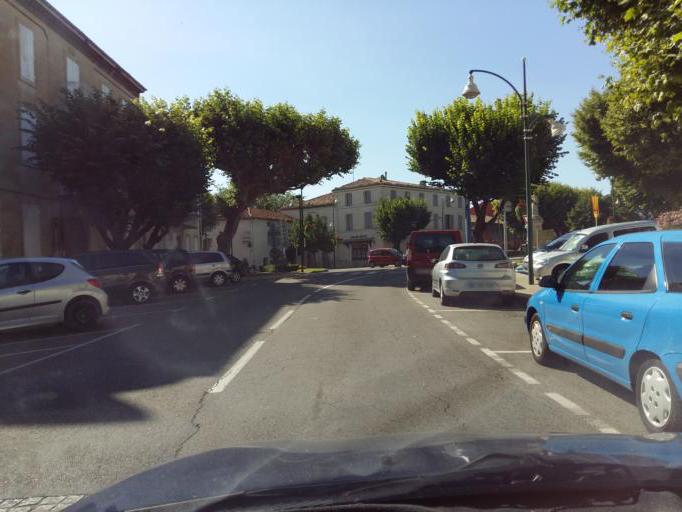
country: FR
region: Provence-Alpes-Cote d'Azur
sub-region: Departement du Vaucluse
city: Valreas
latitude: 44.3826
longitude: 4.9882
